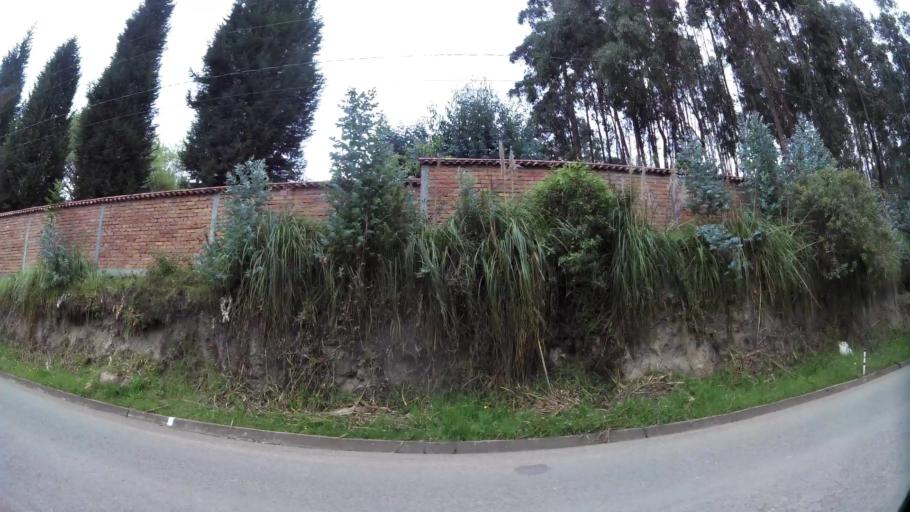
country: EC
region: Azuay
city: Cuenca
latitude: -2.8807
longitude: -79.0711
